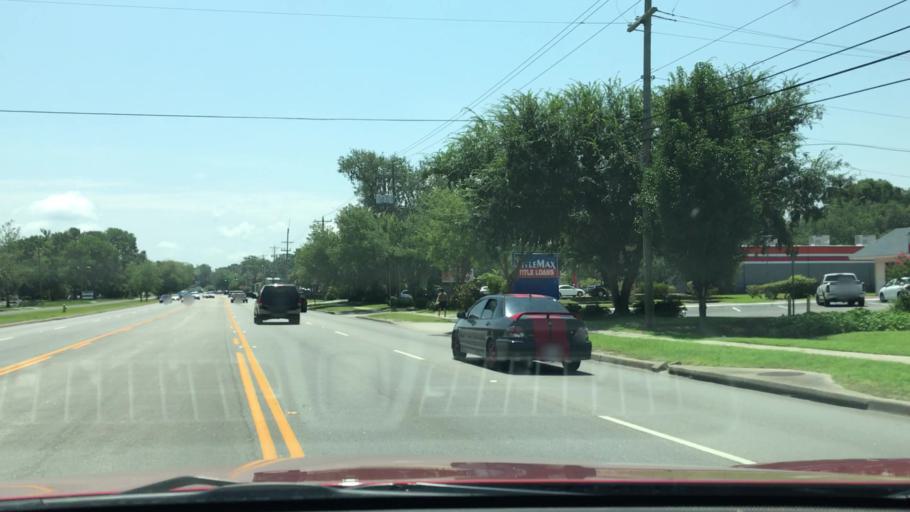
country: US
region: South Carolina
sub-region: Berkeley County
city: Hanahan
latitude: 32.8599
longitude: -80.0460
